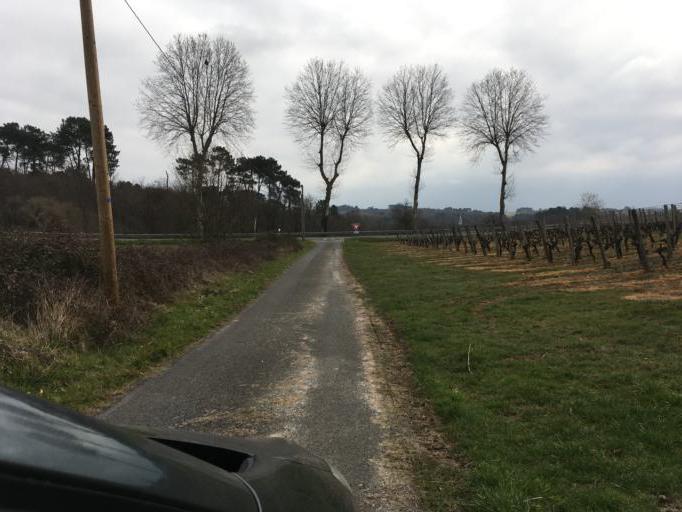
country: FR
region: Poitou-Charentes
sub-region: Departement de la Charente-Maritime
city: Mirambeau
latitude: 45.3352
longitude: -0.5784
